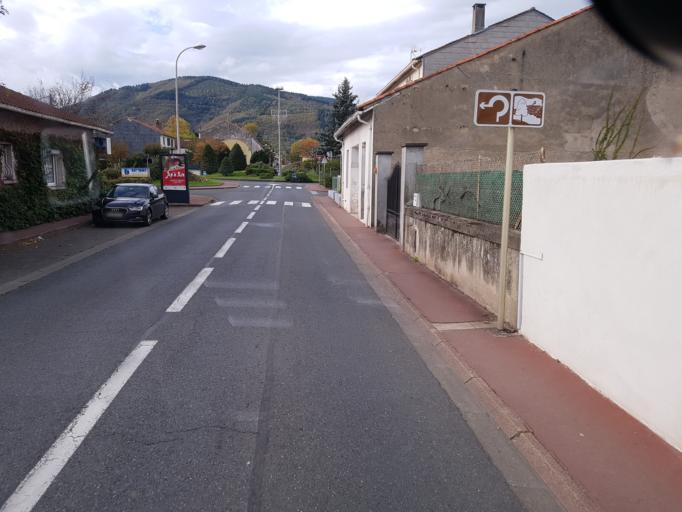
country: FR
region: Midi-Pyrenees
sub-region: Departement du Tarn
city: Mazamet
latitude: 43.4970
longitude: 2.3825
